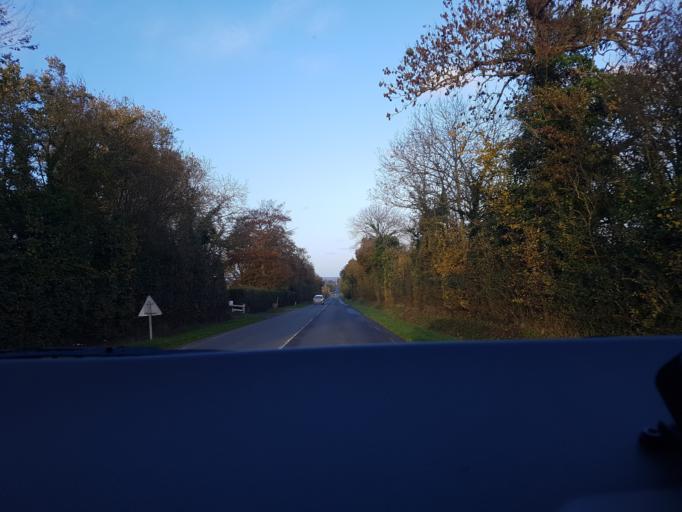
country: FR
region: Lower Normandy
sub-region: Departement du Calvados
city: Troarn
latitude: 49.1967
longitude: -0.1348
